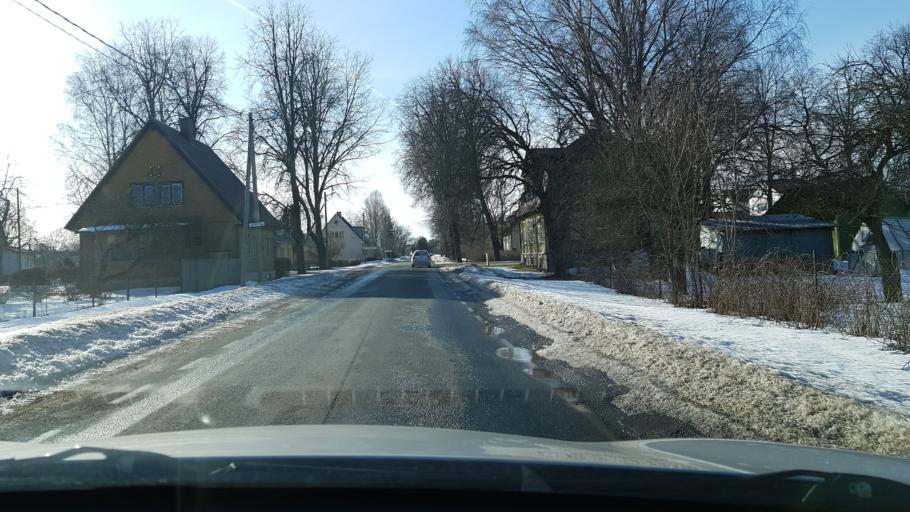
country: EE
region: Viljandimaa
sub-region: Suure-Jaani vald
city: Suure-Jaani
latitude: 58.5399
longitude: 25.4733
